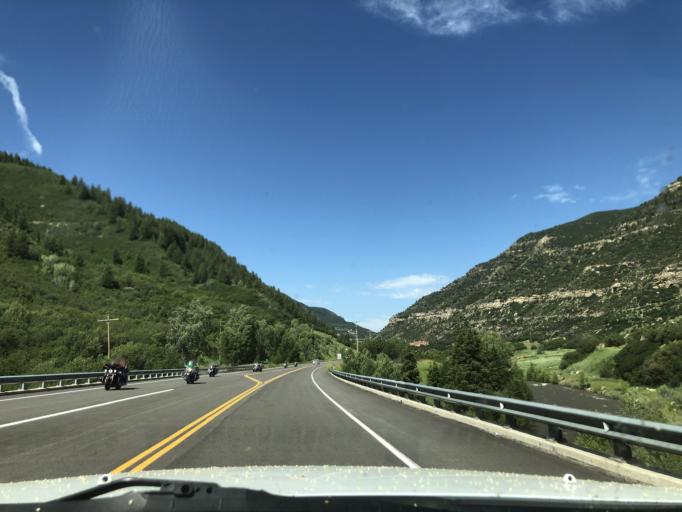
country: US
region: Colorado
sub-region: Delta County
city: Paonia
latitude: 38.9312
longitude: -107.4081
